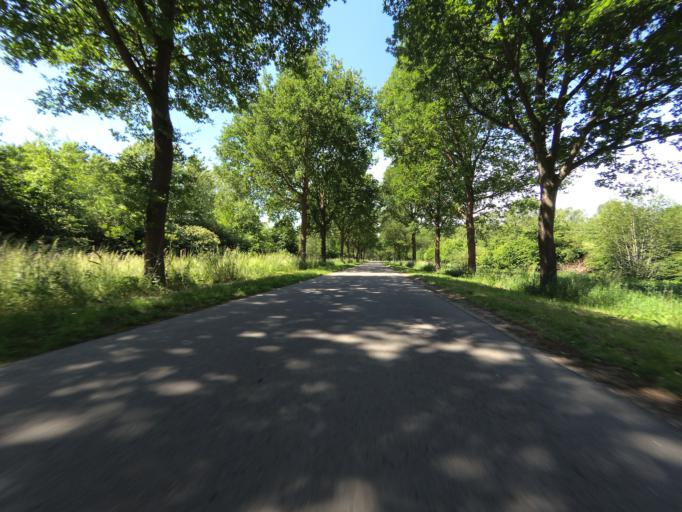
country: NL
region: Flevoland
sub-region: Gemeente Zeewolde
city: Zeewolde
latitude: 52.3419
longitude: 5.5032
